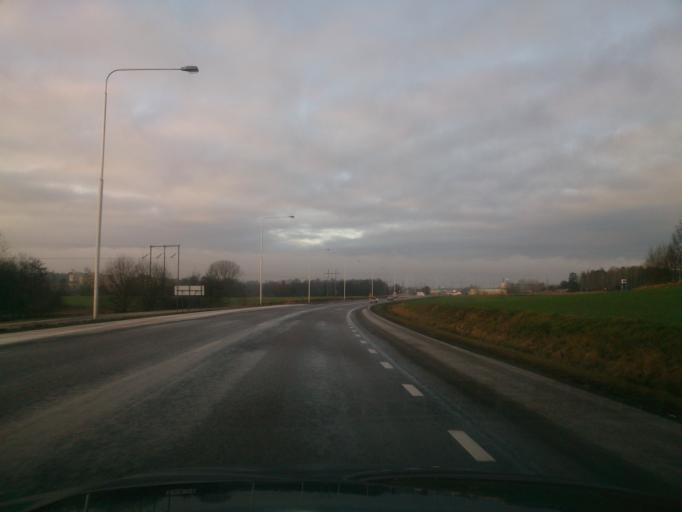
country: SE
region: OEstergoetland
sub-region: Linkopings Kommun
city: Linkoping
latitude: 58.3995
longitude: 15.6818
